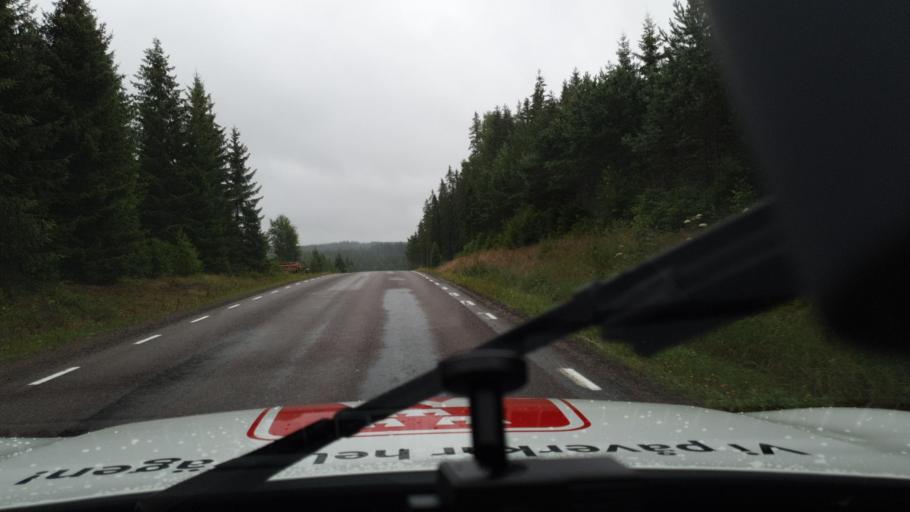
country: SE
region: Vaermland
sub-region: Torsby Kommun
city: Torsby
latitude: 59.9328
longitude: 12.7991
